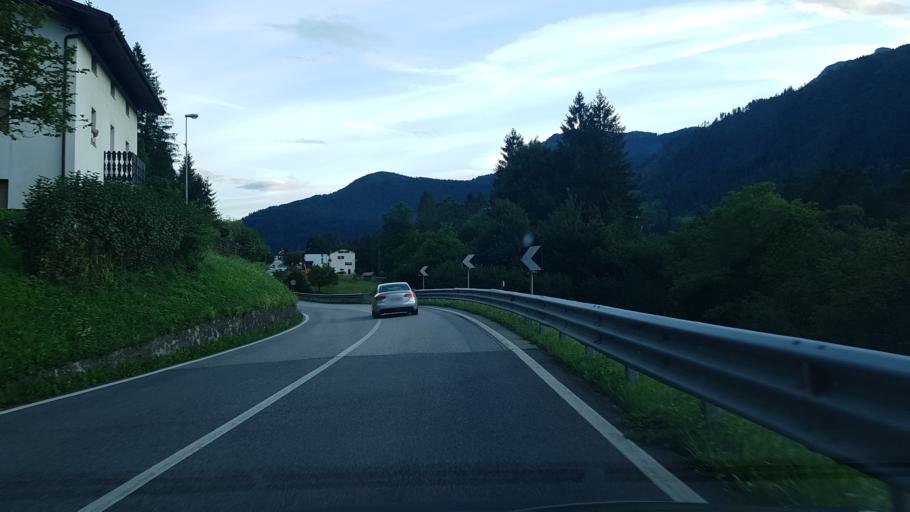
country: IT
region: Friuli Venezia Giulia
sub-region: Provincia di Udine
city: Ovaro
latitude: 46.4961
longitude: 12.8666
